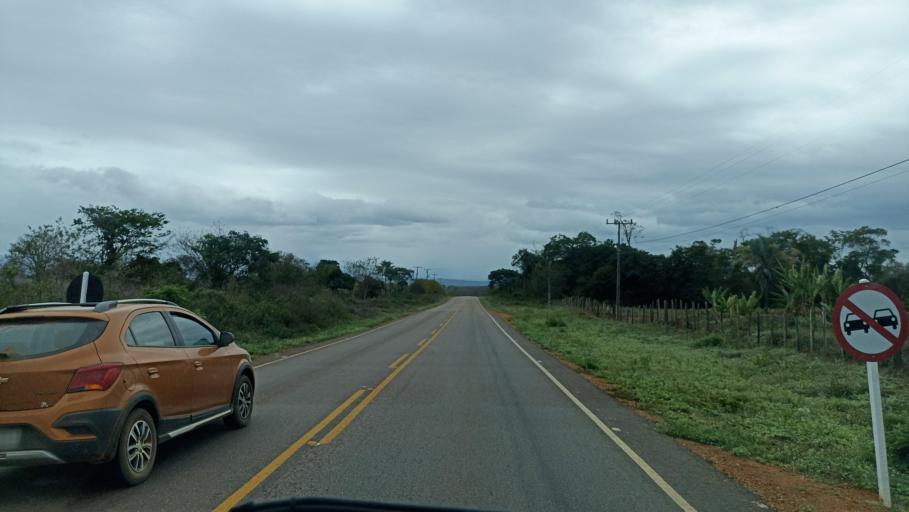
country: BR
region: Bahia
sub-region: Andarai
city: Vera Cruz
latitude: -12.9880
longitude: -41.0055
